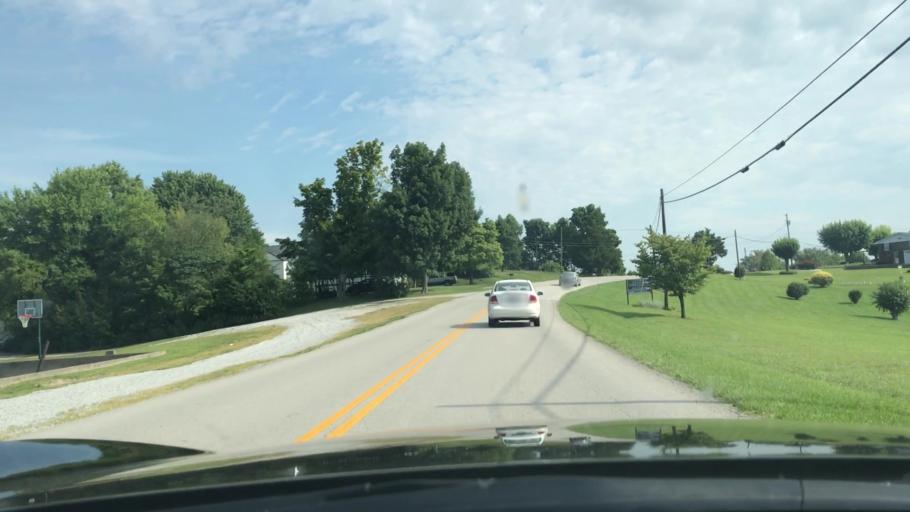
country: US
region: Kentucky
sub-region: Green County
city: Greensburg
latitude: 37.2801
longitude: -85.5220
